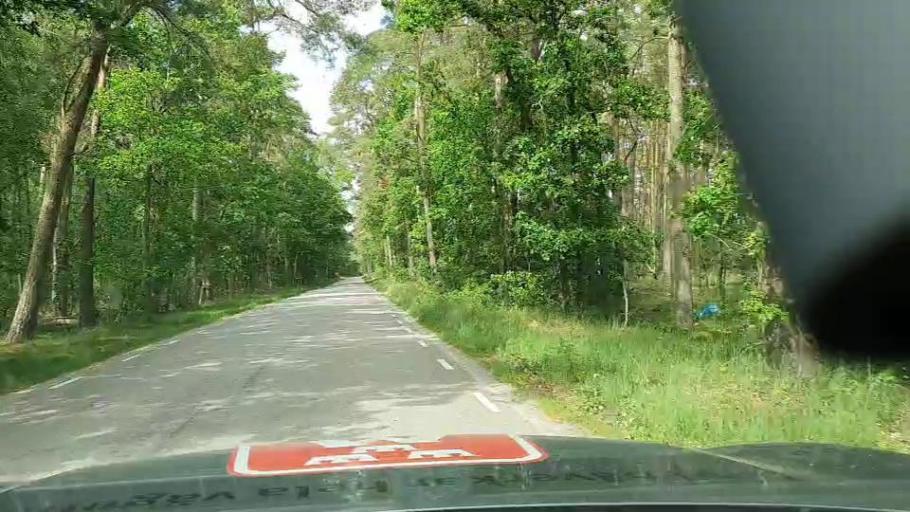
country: SE
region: Blekinge
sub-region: Karlshamns Kommun
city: Morrum
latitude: 56.0991
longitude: 14.6875
